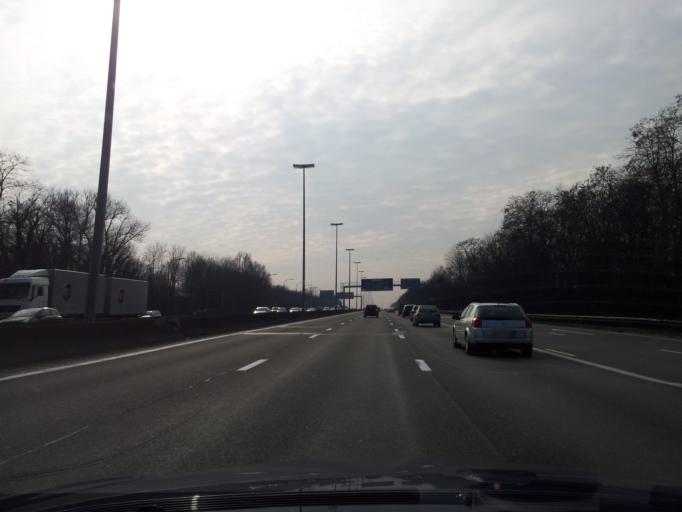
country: BE
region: Flanders
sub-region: Provincie Vlaams-Brabant
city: Zaventem
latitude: 50.8780
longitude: 4.4626
